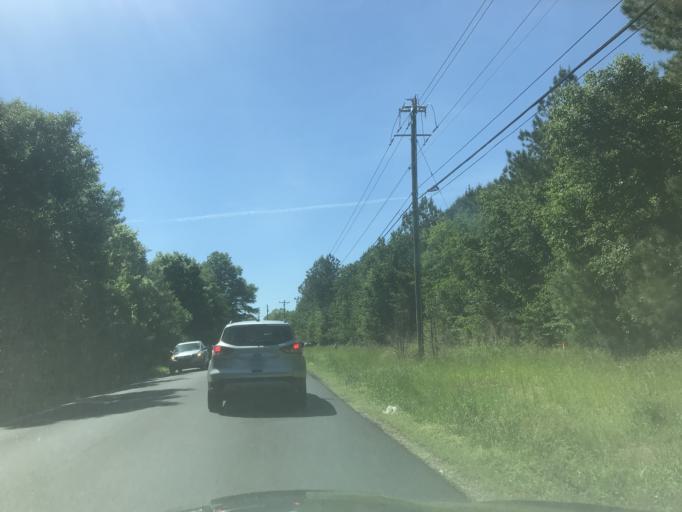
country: US
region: North Carolina
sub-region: Wake County
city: West Raleigh
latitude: 35.7427
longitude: -78.6770
